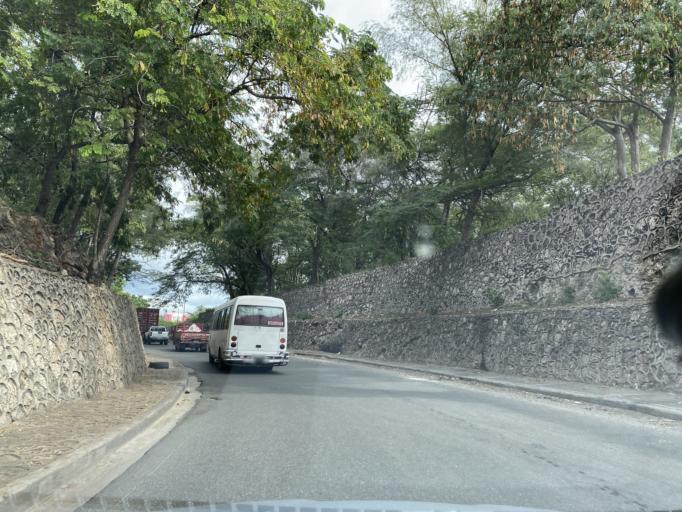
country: DO
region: Santo Domingo
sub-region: Santo Domingo
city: Santo Domingo Este
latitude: 18.4839
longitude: -69.8538
